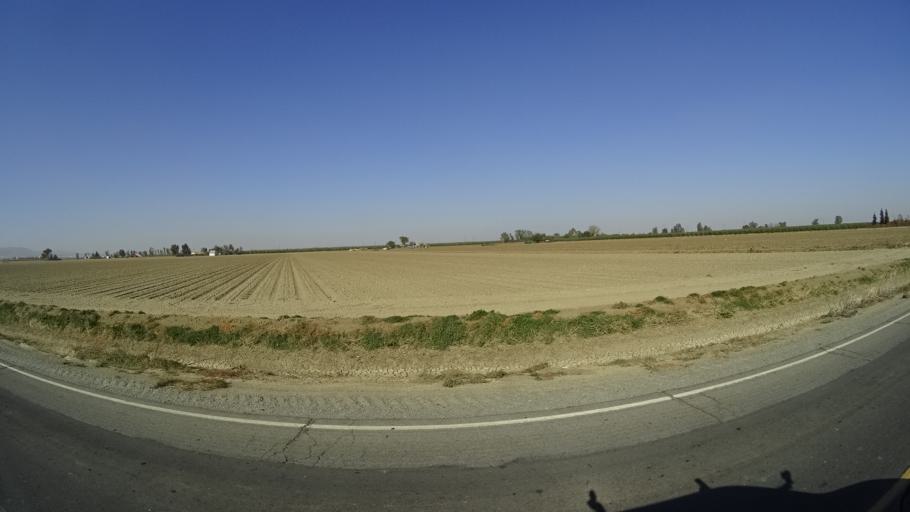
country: US
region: California
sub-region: Yolo County
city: Esparto
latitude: 38.7315
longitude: -121.9940
